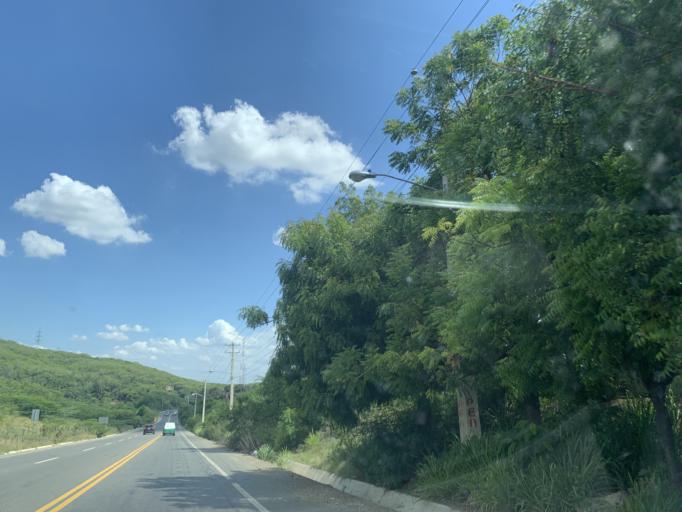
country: DO
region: Santiago
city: Villa Bisono
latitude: 19.5846
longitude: -70.8460
